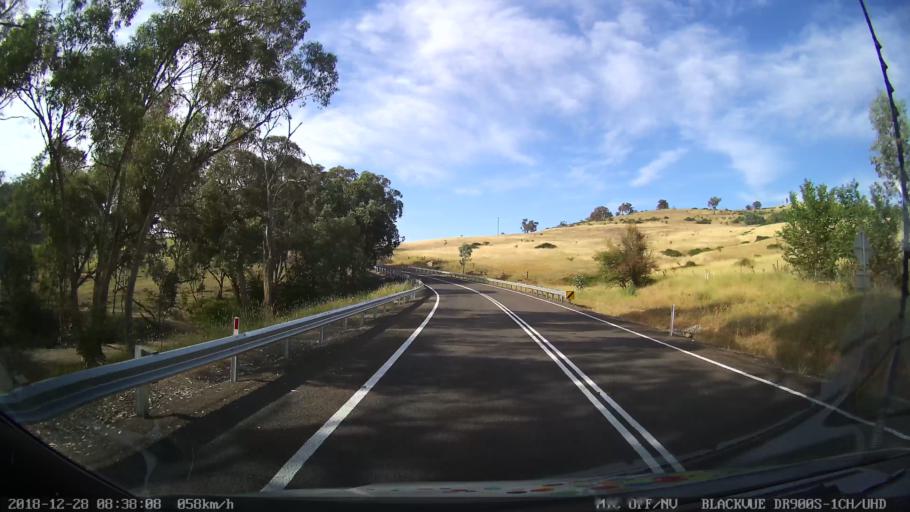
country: AU
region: New South Wales
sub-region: Blayney
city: Blayney
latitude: -34.0011
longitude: 149.3146
